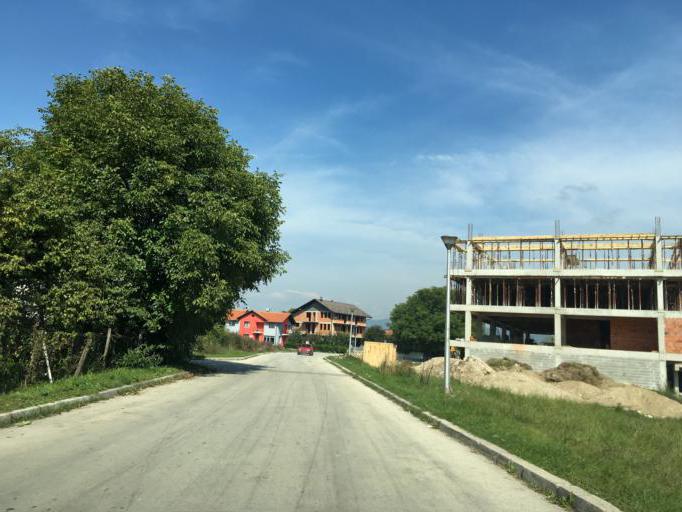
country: BA
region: Federation of Bosnia and Herzegovina
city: Bugojno
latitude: 44.0534
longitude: 17.4529
